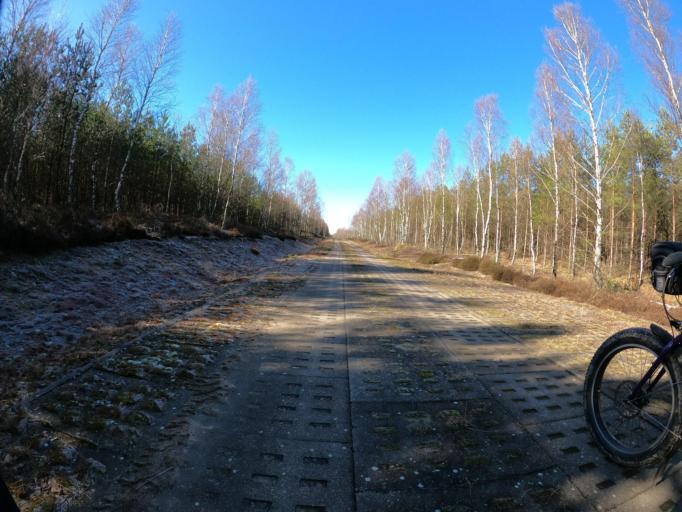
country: PL
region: Greater Poland Voivodeship
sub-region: Powiat zlotowski
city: Sypniewo
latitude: 53.5328
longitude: 16.6164
